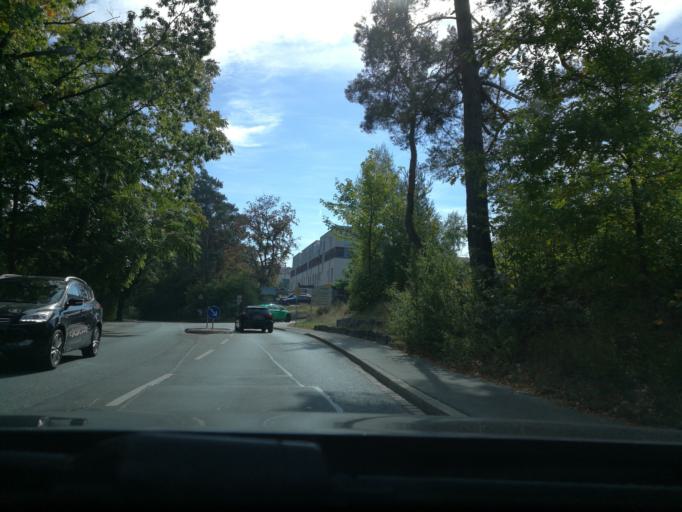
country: DE
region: Bavaria
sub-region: Regierungsbezirk Mittelfranken
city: Furth
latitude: 49.5022
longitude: 10.9680
